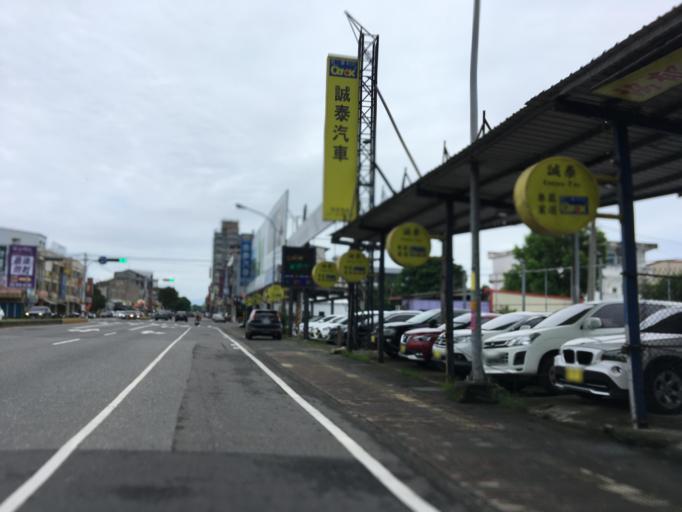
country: TW
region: Taiwan
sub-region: Yilan
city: Yilan
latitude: 24.7049
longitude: 121.7710
